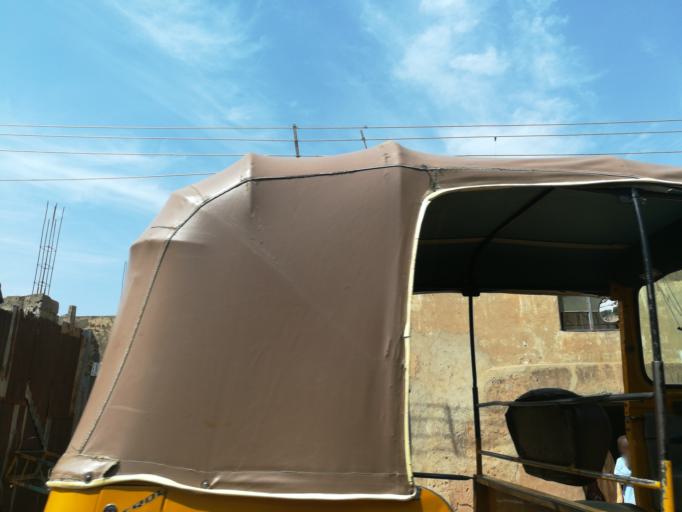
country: NG
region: Kano
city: Kano
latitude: 12.0156
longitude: 8.5113
